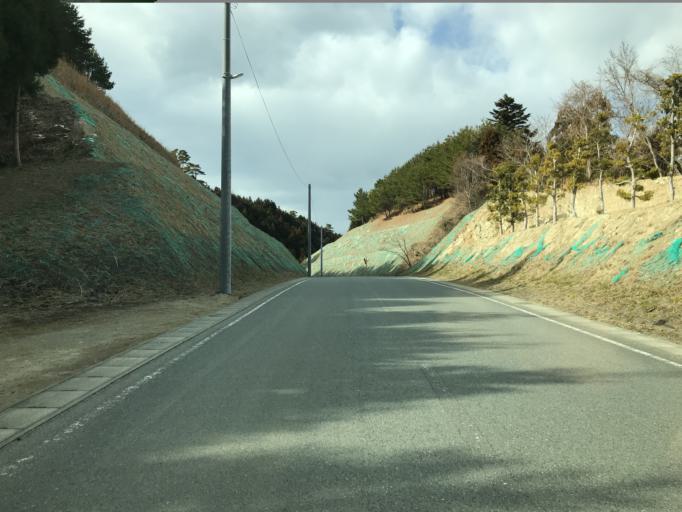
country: JP
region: Fukushima
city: Iwaki
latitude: 37.1651
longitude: 140.9982
